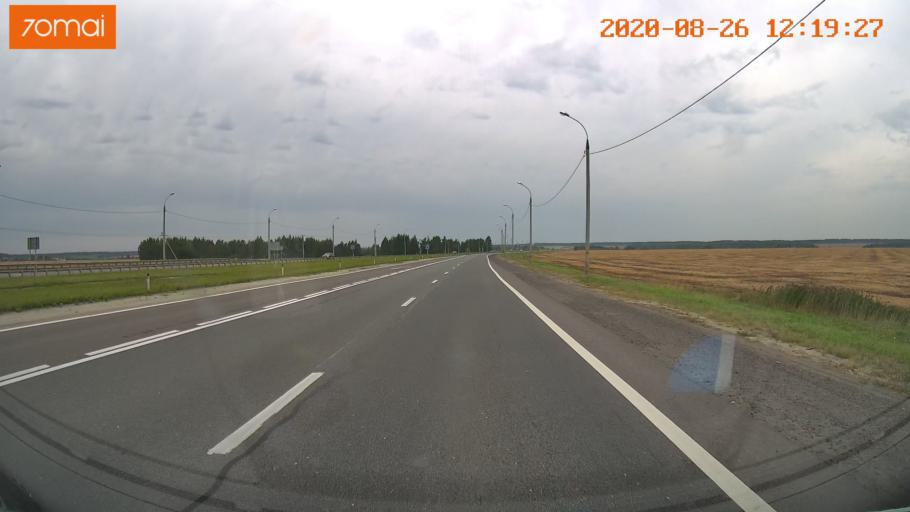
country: RU
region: Rjazan
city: Murmino
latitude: 54.4754
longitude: 39.9980
